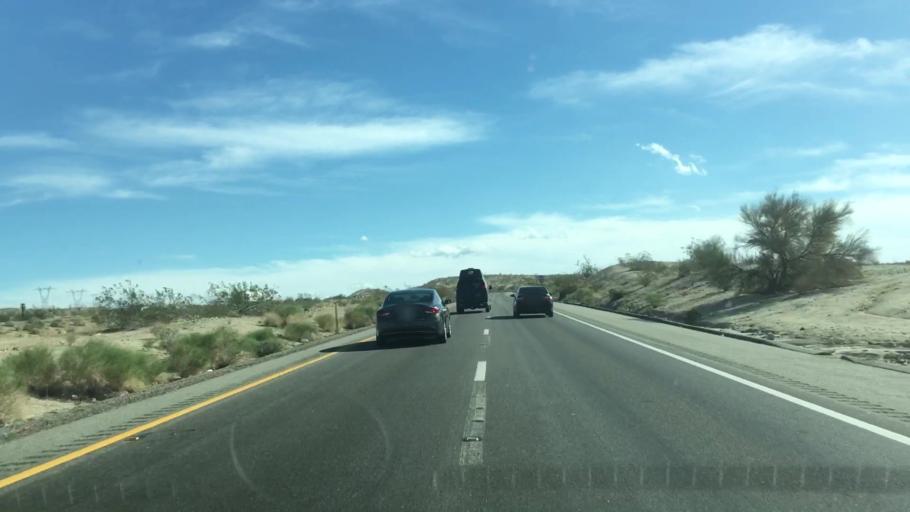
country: US
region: California
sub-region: Riverside County
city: Thermal
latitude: 33.6944
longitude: -116.0551
